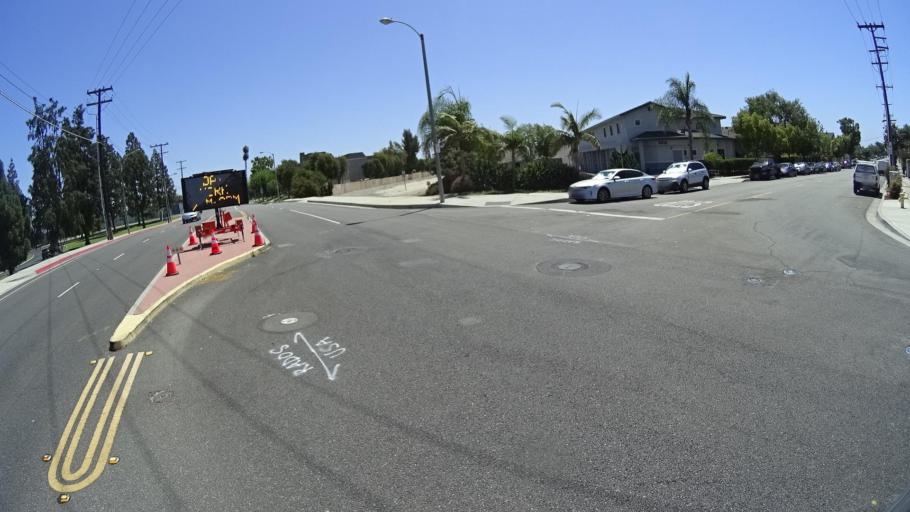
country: US
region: California
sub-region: Orange County
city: Cypress
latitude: 33.8246
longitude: -118.0241
